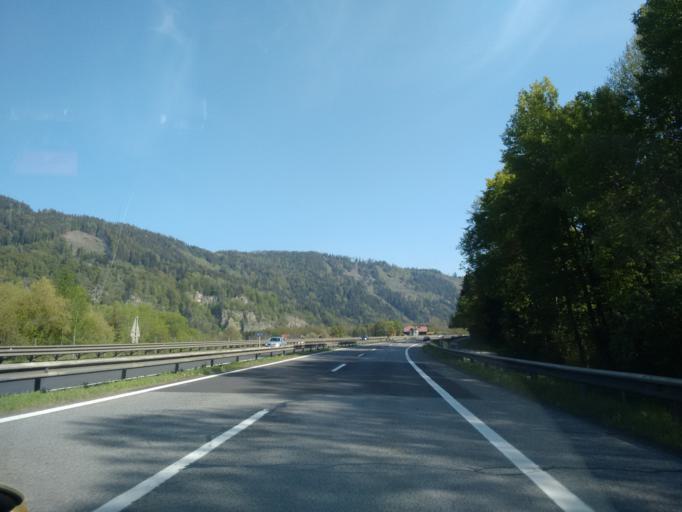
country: AT
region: Styria
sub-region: Politischer Bezirk Leoben
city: Leoben
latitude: 47.3453
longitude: 15.0559
